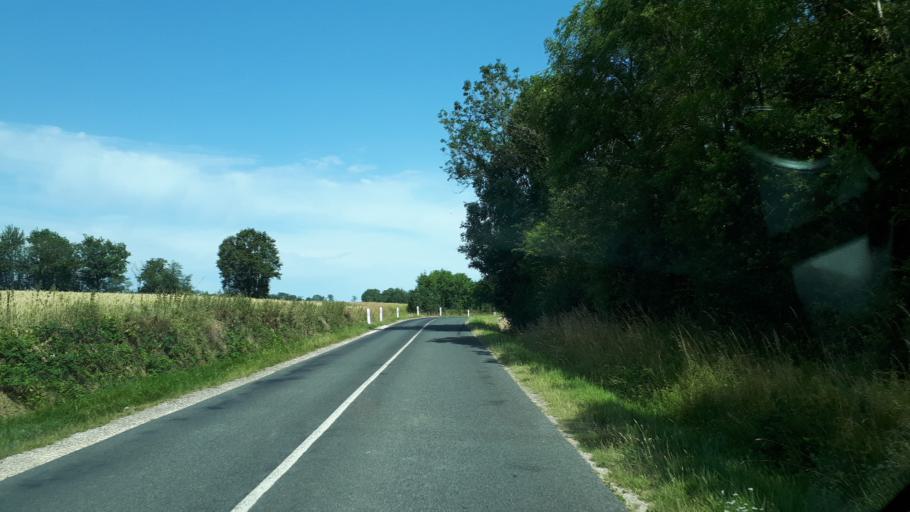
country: FR
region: Centre
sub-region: Departement du Loir-et-Cher
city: La Ville-aux-Clercs
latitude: 47.9338
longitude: 1.0832
